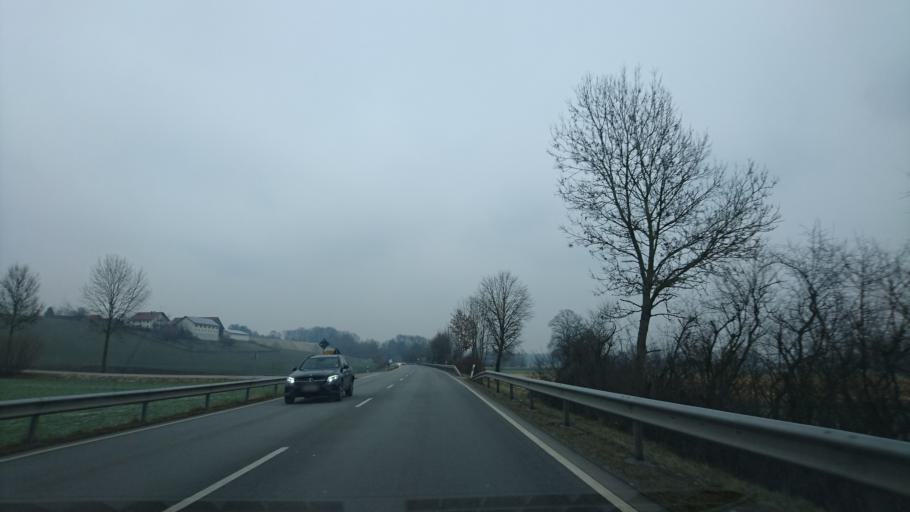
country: DE
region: Bavaria
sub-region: Lower Bavaria
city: Tettenweis
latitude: 48.4136
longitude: 13.2659
